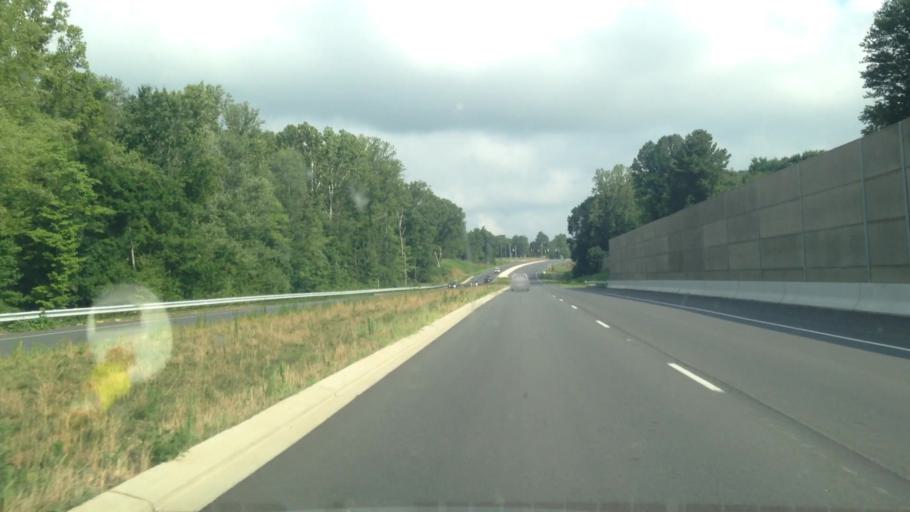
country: US
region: North Carolina
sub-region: Guilford County
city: Summerfield
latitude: 36.2042
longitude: -79.9008
